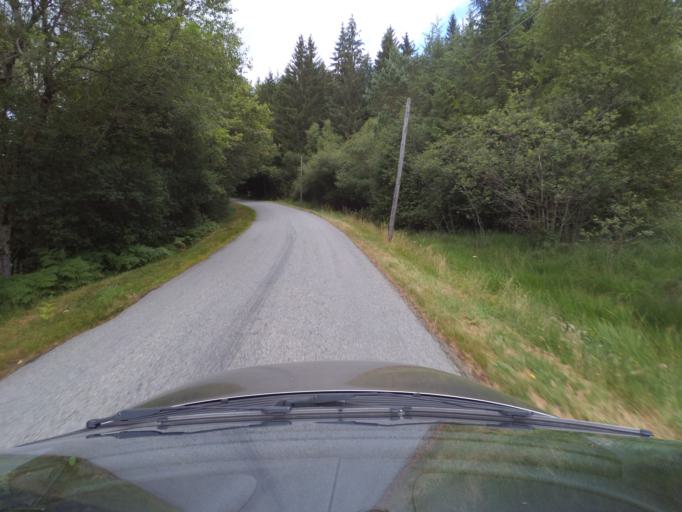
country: FR
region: Limousin
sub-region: Departement de la Haute-Vienne
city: Peyrat-le-Chateau
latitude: 45.8261
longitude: 1.9179
